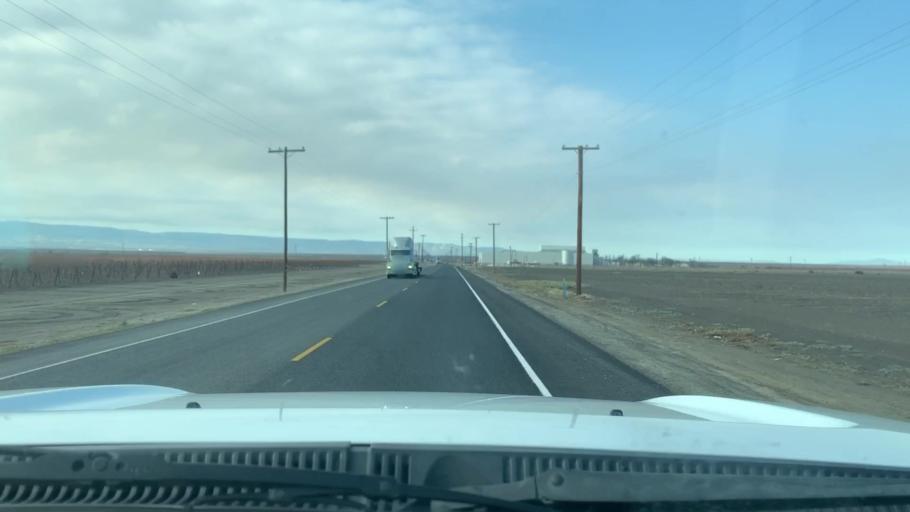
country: US
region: California
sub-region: Kern County
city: Lost Hills
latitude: 35.4995
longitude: -119.5965
